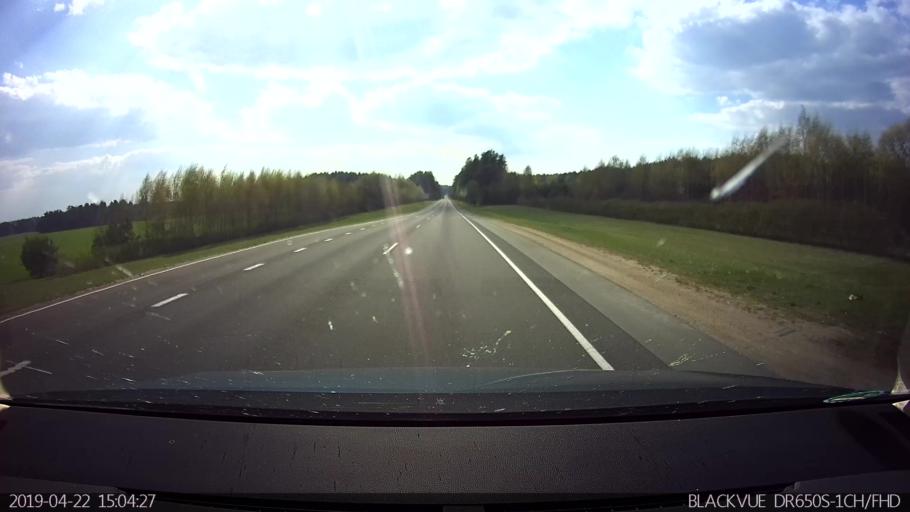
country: BY
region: Brest
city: Kamyanyets
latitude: 52.3399
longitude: 23.8950
